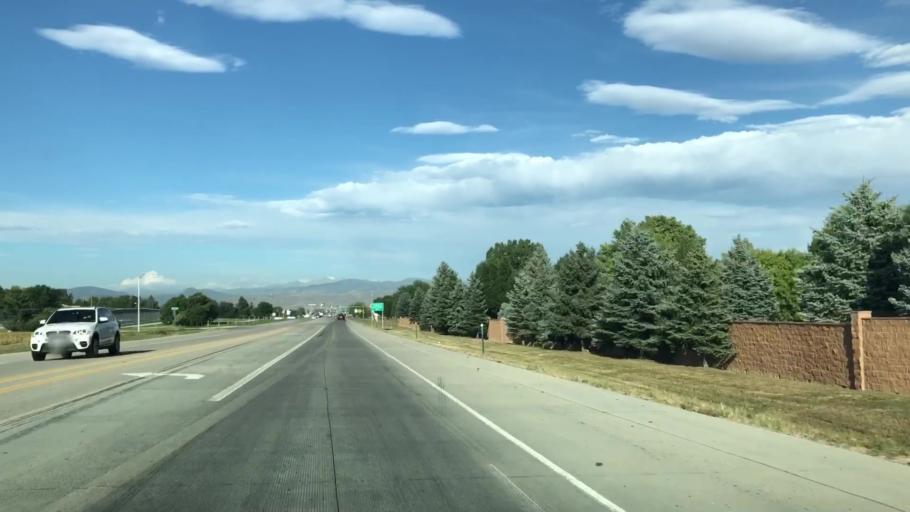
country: US
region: Colorado
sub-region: Weld County
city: Windsor
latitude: 40.4795
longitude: -104.9771
